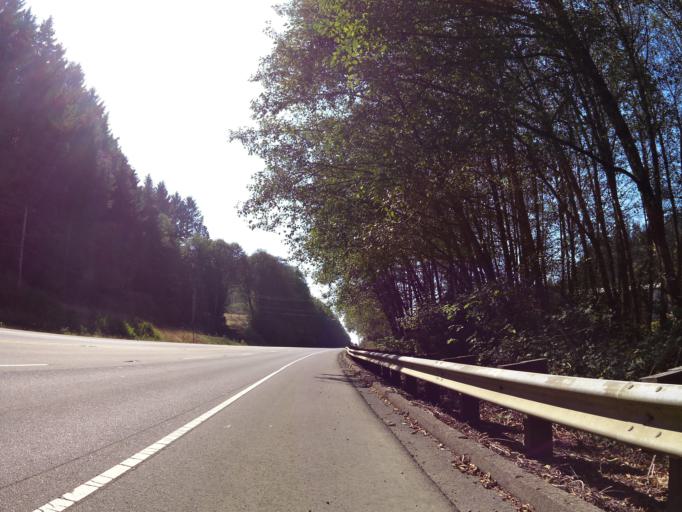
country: US
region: Oregon
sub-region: Tillamook County
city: Pacific City
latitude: 45.1486
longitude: -123.9597
